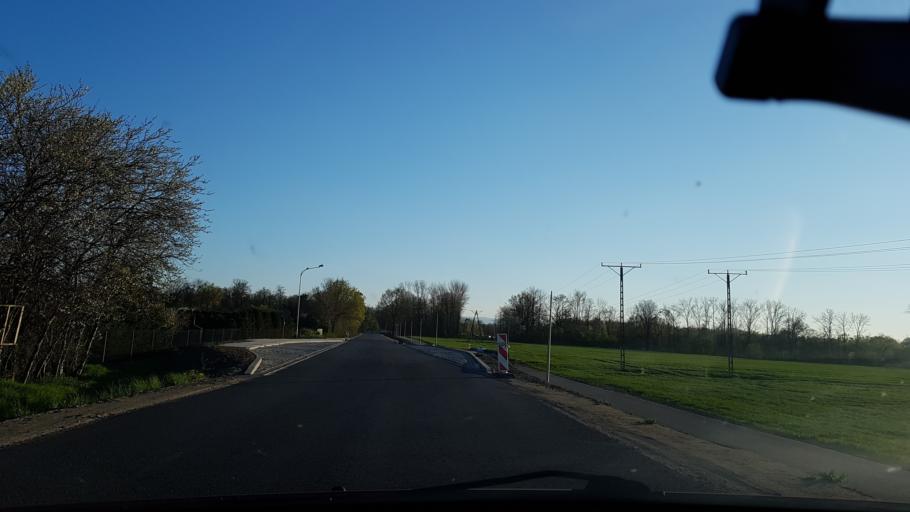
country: PL
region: Opole Voivodeship
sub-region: Powiat nyski
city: Nysa
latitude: 50.4384
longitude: 17.3045
